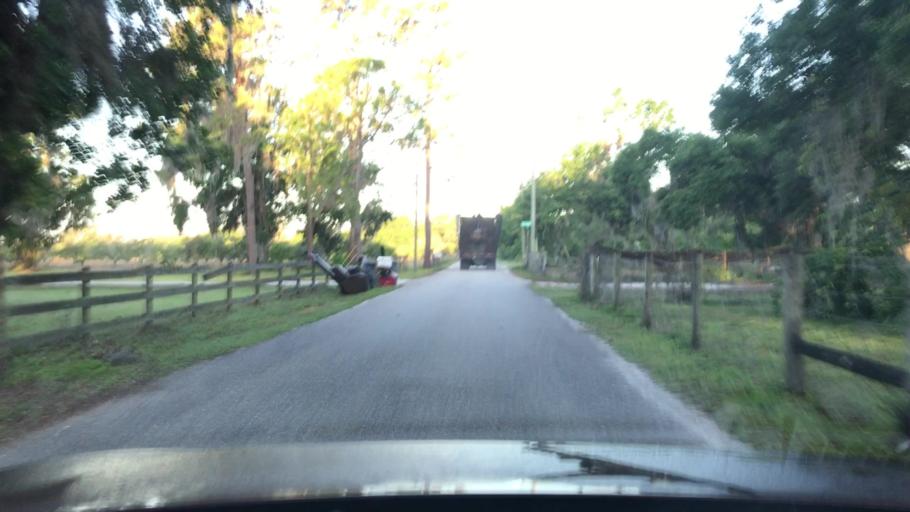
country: US
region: Florida
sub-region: Sarasota County
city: Fruitville
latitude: 27.3309
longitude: -82.4118
